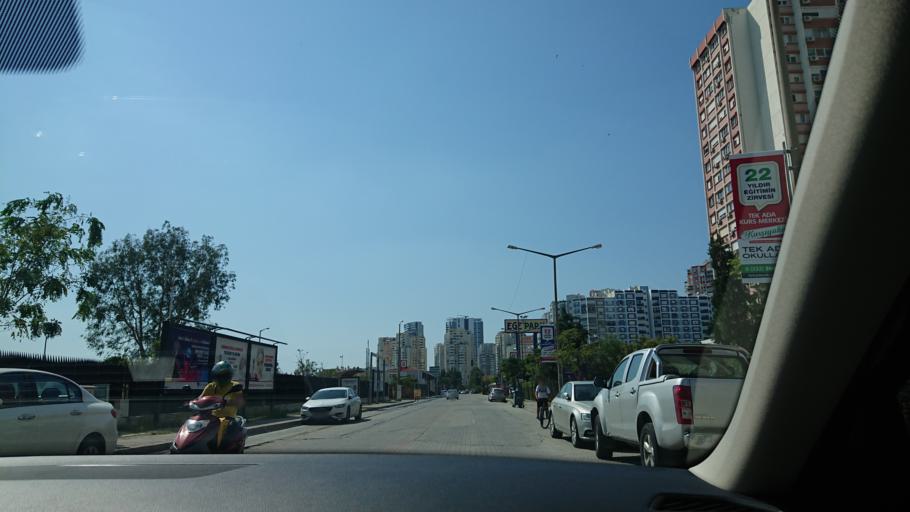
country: TR
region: Izmir
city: Karsiyaka
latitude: 38.4691
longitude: 27.0767
